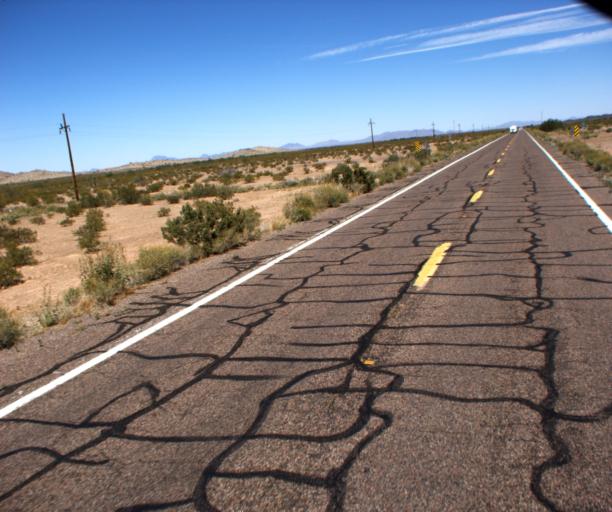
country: US
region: Arizona
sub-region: Maricopa County
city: Gila Bend
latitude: 32.7656
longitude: -112.8187
